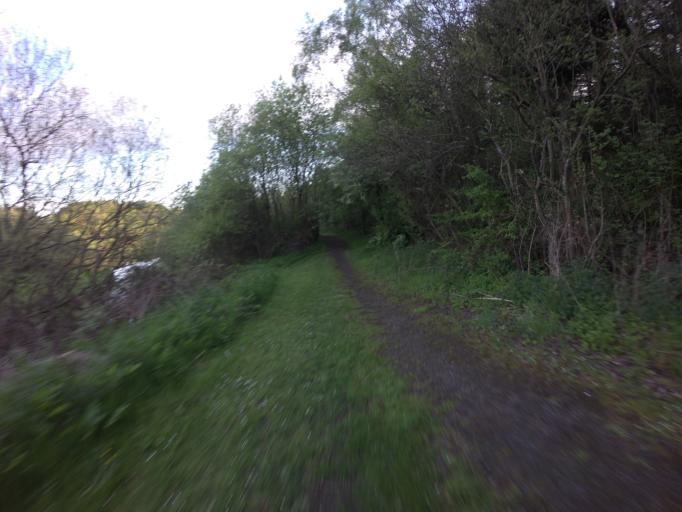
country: GB
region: Scotland
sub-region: West Lothian
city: West Calder
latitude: 55.8834
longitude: -3.5606
